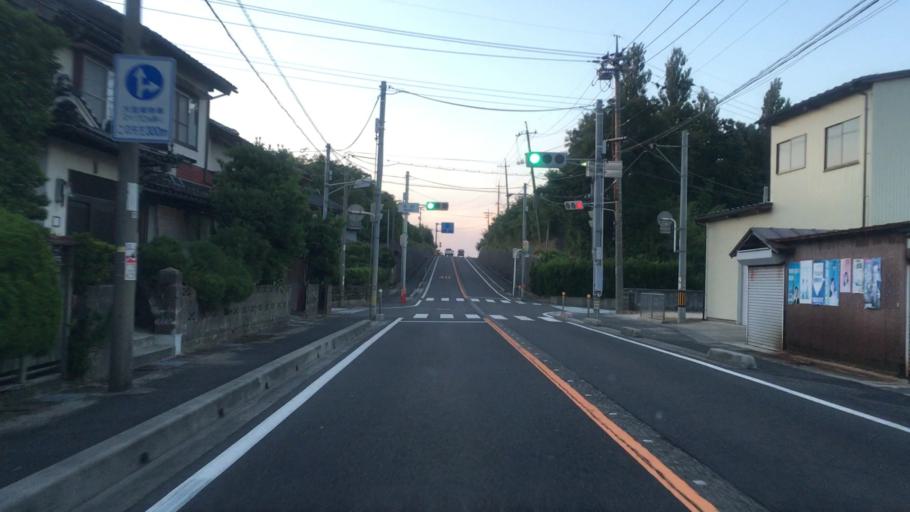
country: JP
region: Tottori
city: Tottori
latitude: 35.5863
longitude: 134.3326
